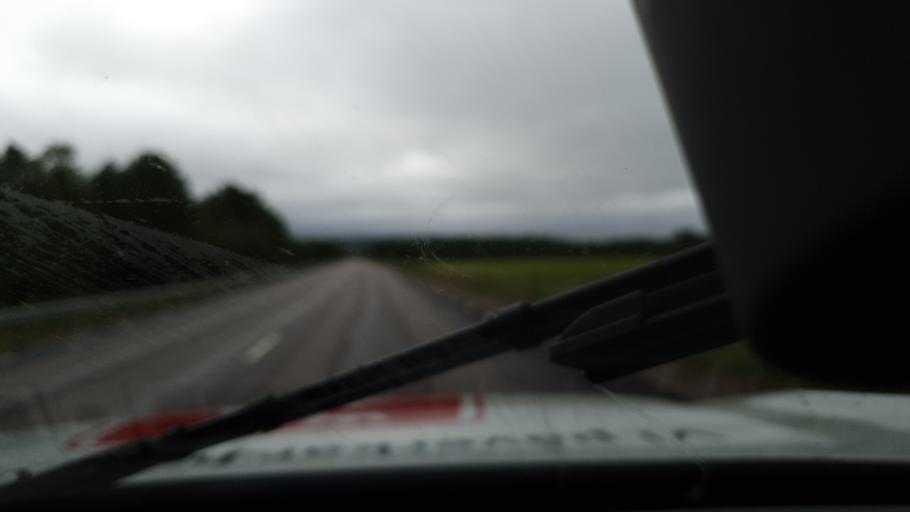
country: SE
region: Norrbotten
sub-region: Overtornea Kommun
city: OEvertornea
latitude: 66.4150
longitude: 23.6249
